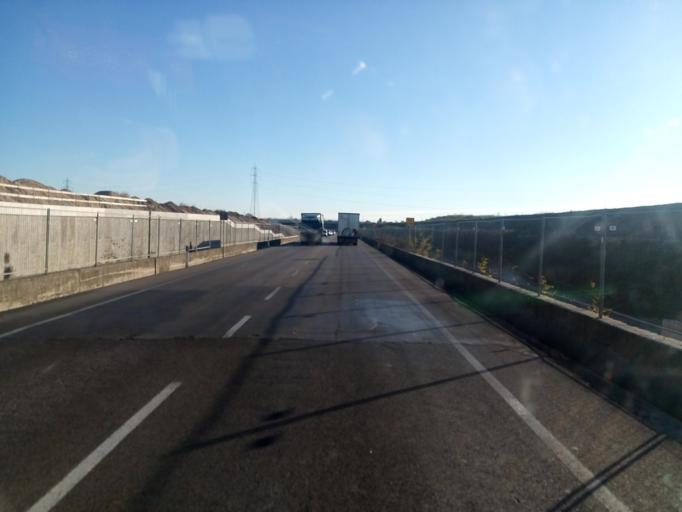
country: IT
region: Veneto
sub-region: Provincia di Vicenza
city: San Zeno-San Giuseppe
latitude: 45.7361
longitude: 11.7450
